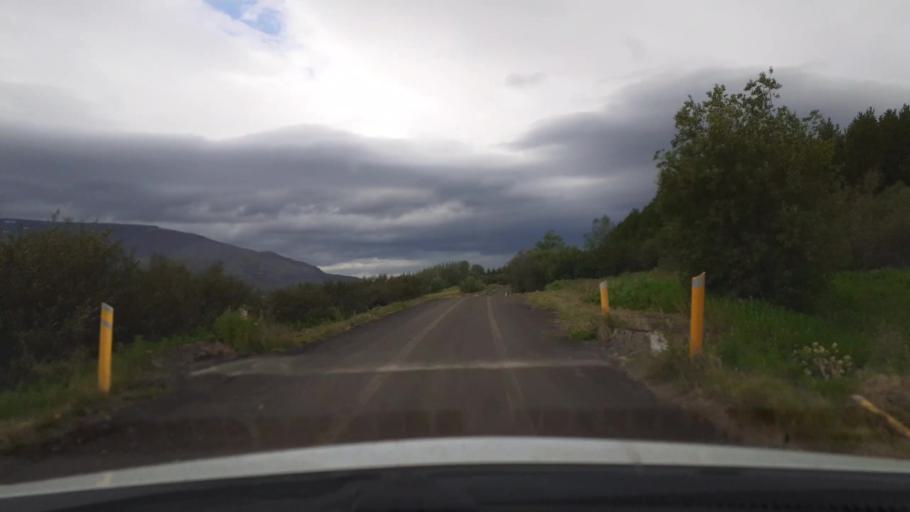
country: IS
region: Capital Region
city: Mosfellsbaer
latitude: 64.5213
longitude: -21.4599
